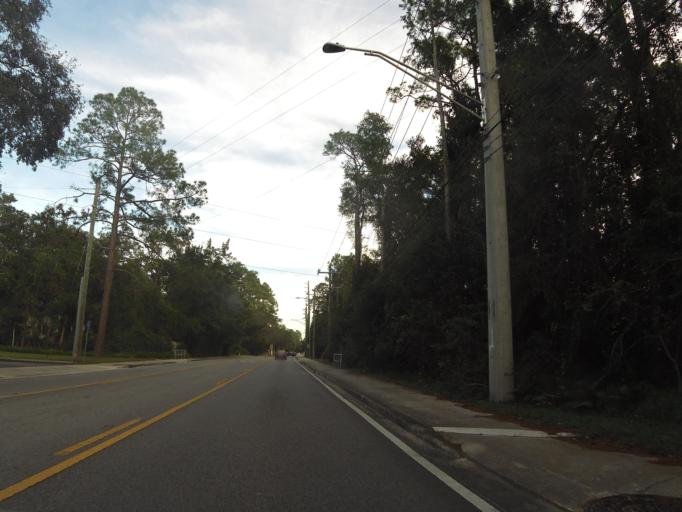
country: US
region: Florida
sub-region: Saint Johns County
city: Fruit Cove
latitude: 30.1598
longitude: -81.6211
